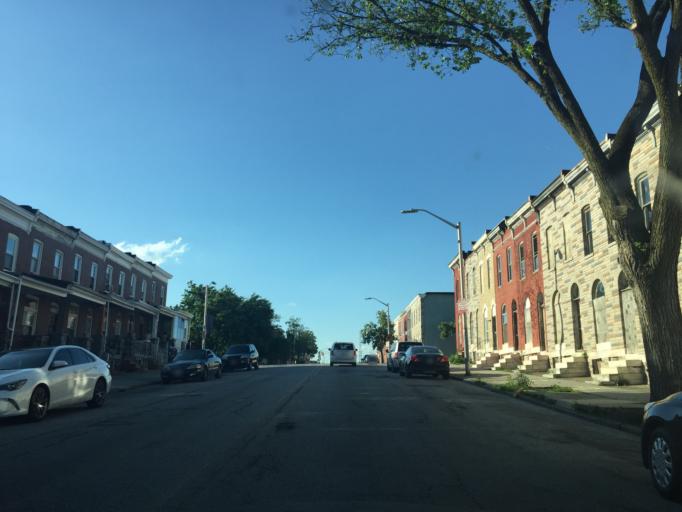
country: US
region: Maryland
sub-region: City of Baltimore
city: Baltimore
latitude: 39.3074
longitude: -76.5828
